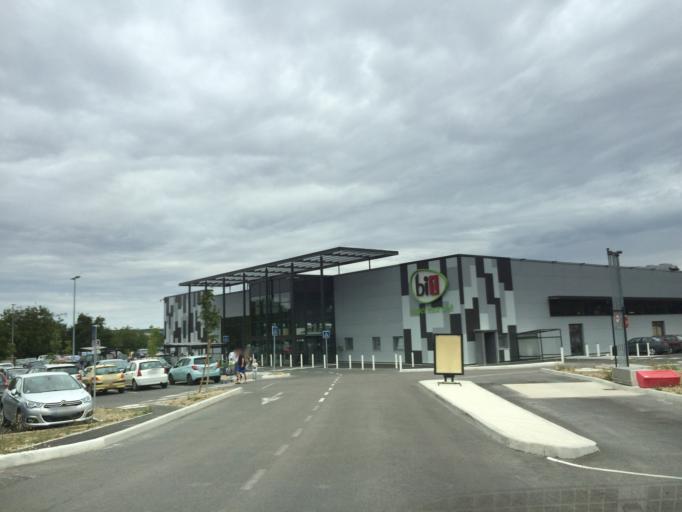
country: FR
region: Bourgogne
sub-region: Departement de l'Yonne
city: Aillant-sur-Tholon
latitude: 47.8764
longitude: 3.3541
